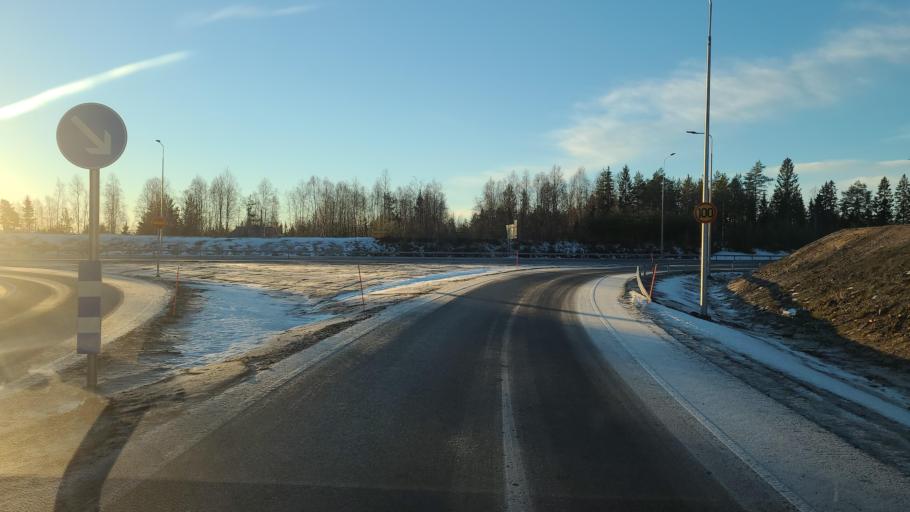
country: FI
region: Lapland
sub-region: Kemi-Tornio
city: Kemi
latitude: 65.6794
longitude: 24.7415
